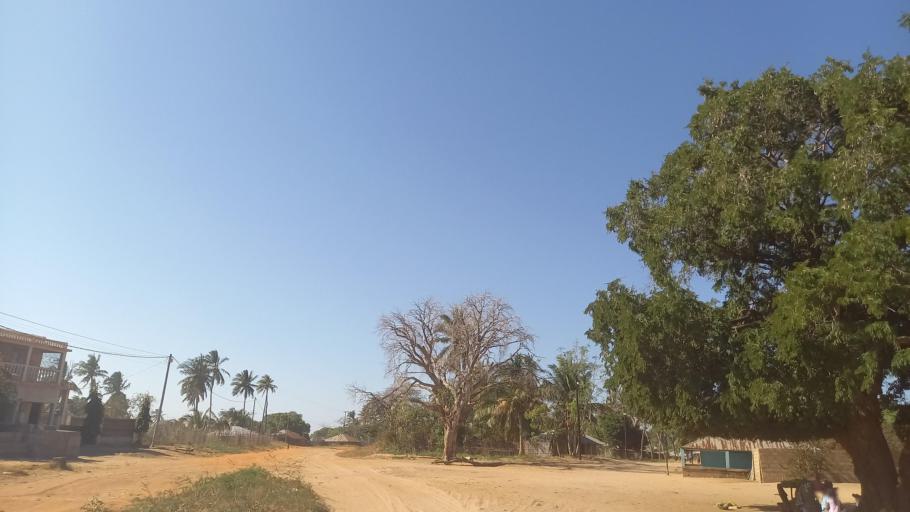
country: MZ
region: Cabo Delgado
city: Pemba
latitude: -13.1429
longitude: 40.5549
